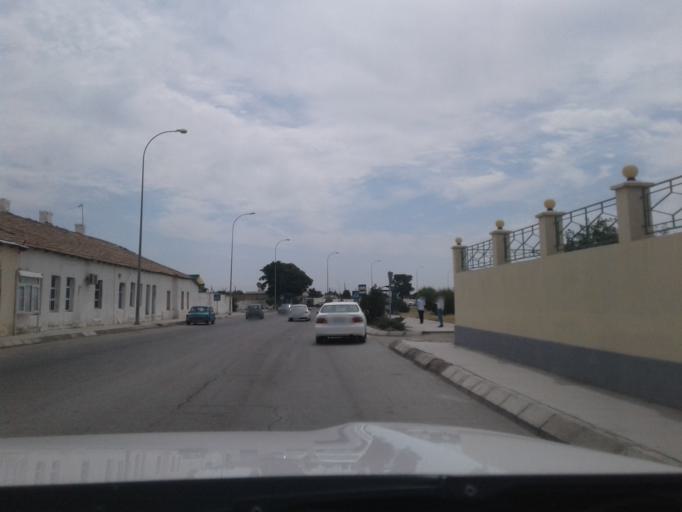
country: TM
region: Balkan
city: Serdar
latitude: 38.9830
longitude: 56.2775
